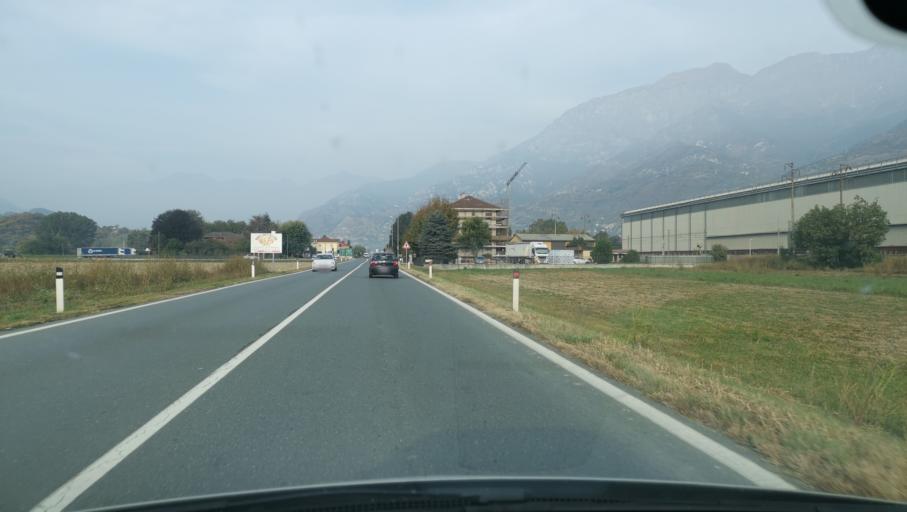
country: IT
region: Piedmont
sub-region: Provincia di Torino
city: San Didero
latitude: 45.1295
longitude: 7.2054
